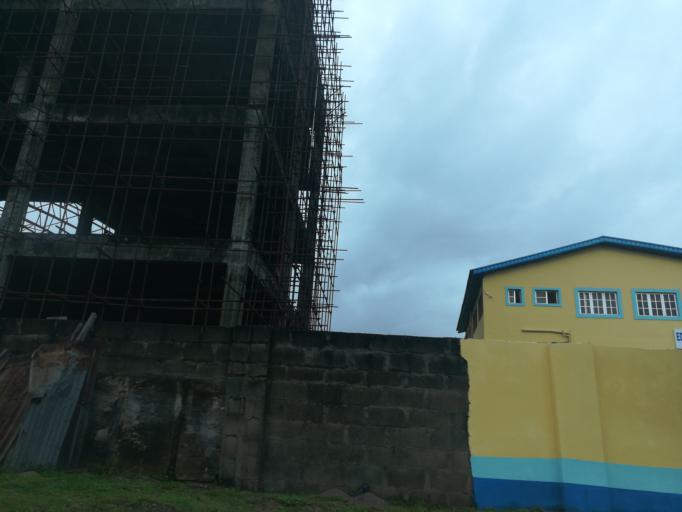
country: NG
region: Lagos
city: Ikeja
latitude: 6.5835
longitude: 3.3340
